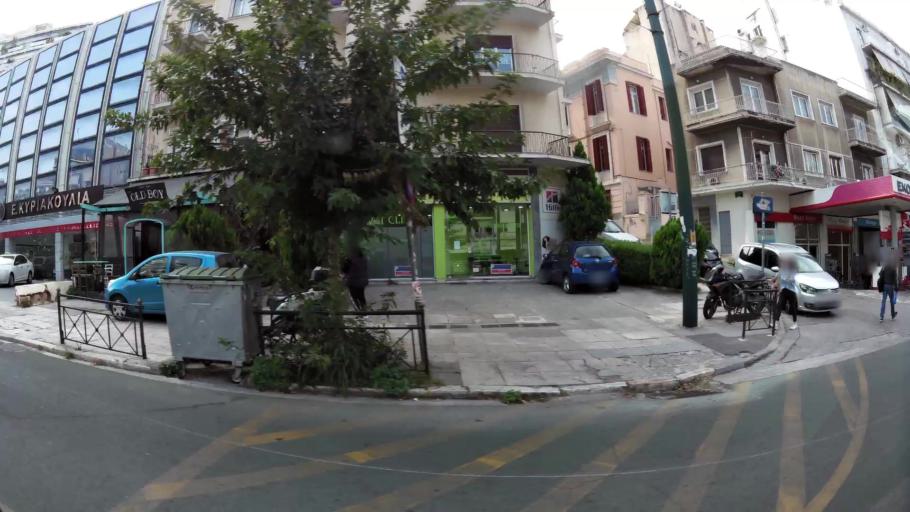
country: GR
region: Attica
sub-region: Nomarchia Athinas
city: Kipseli
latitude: 37.9904
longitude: 23.7390
